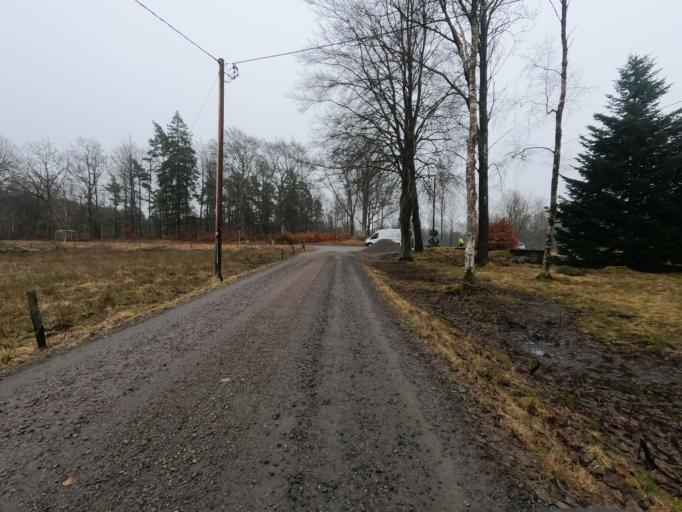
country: SE
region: Halland
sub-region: Hylte Kommun
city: Hyltebruk
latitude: 56.8012
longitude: 13.3312
